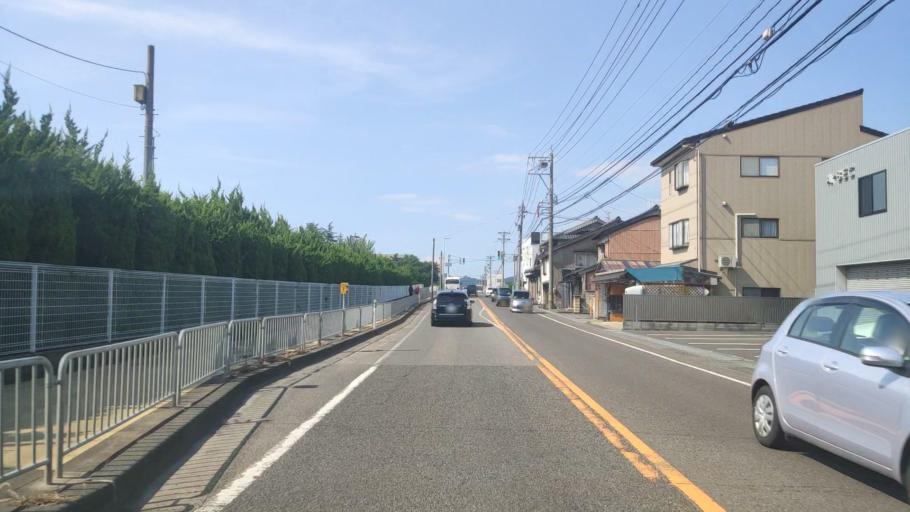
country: JP
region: Fukui
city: Tsuruga
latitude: 35.6408
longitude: 136.0710
